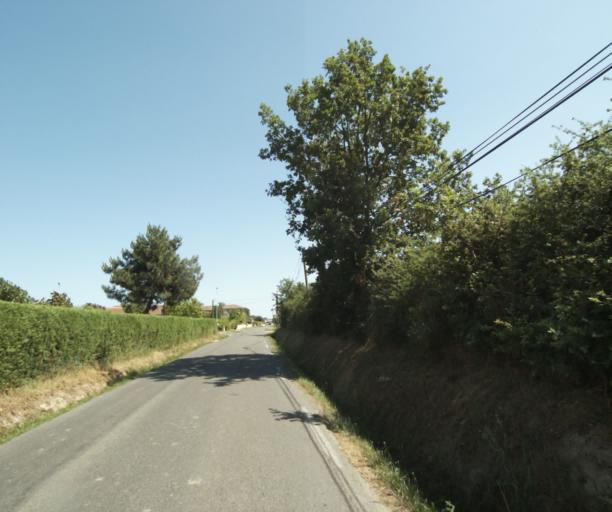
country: FR
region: Midi-Pyrenees
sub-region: Departement du Tarn-et-Garonne
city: Montauban
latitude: 44.0418
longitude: 1.3693
